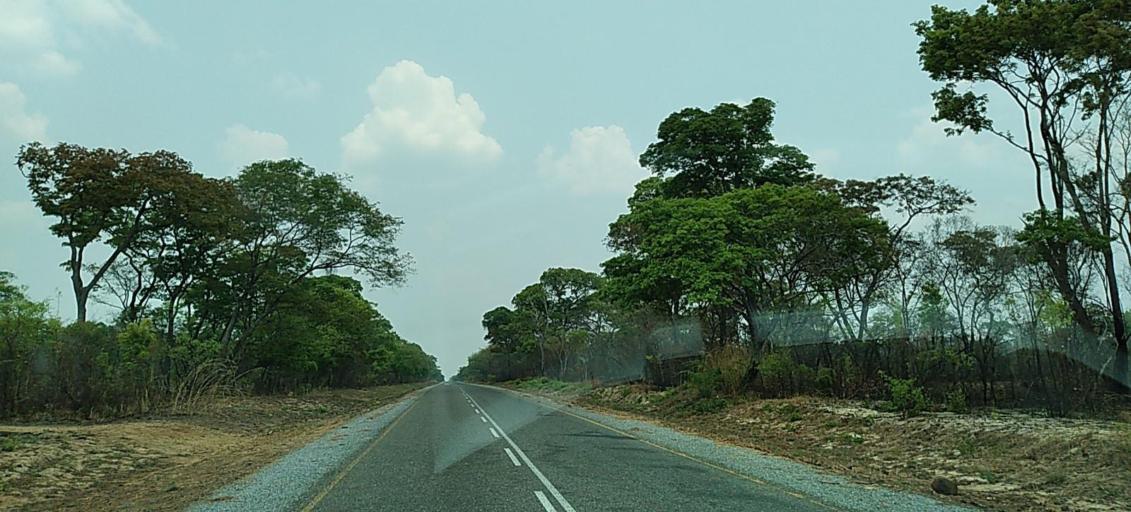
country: ZM
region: North-Western
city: Zambezi
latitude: -13.5691
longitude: 23.2276
